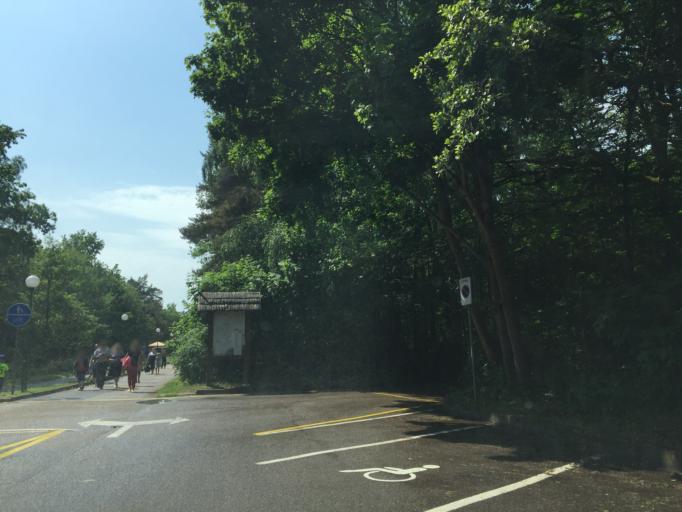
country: LT
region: Klaipedos apskritis
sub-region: Klaipeda
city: Klaipeda
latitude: 55.7658
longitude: 21.0841
